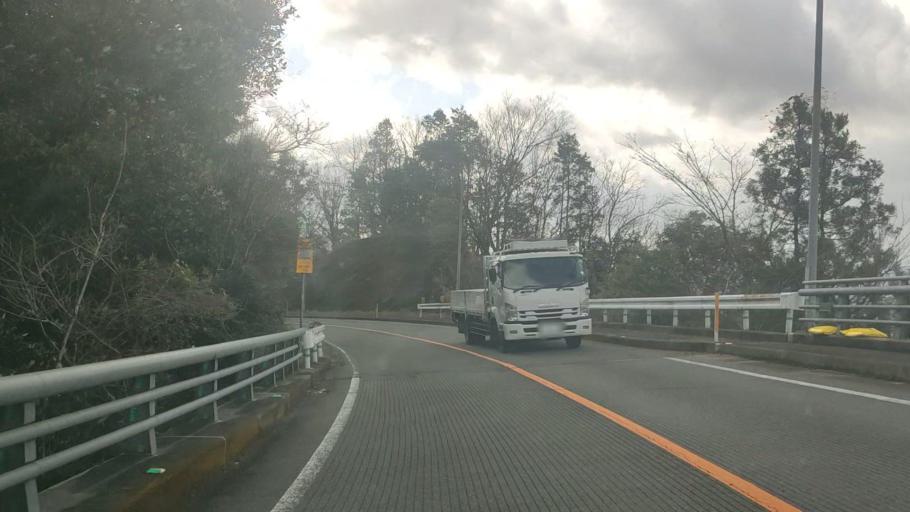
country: JP
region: Kumamoto
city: Hitoyoshi
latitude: 32.0728
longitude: 130.7976
